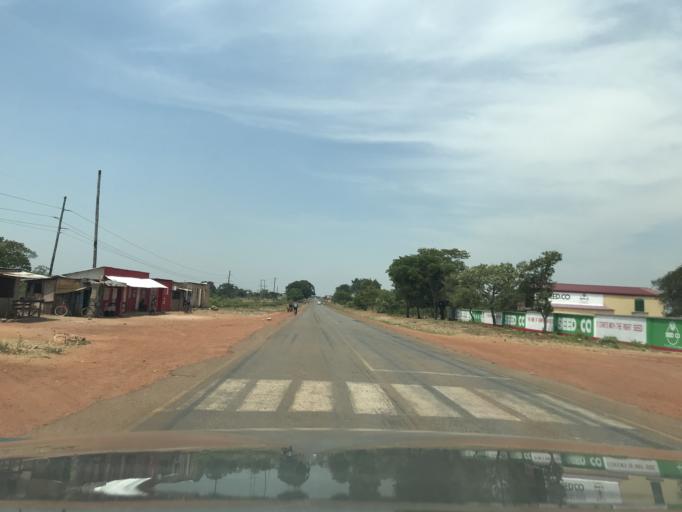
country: ZM
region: Northern
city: Kasama
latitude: -10.2156
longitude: 31.1498
